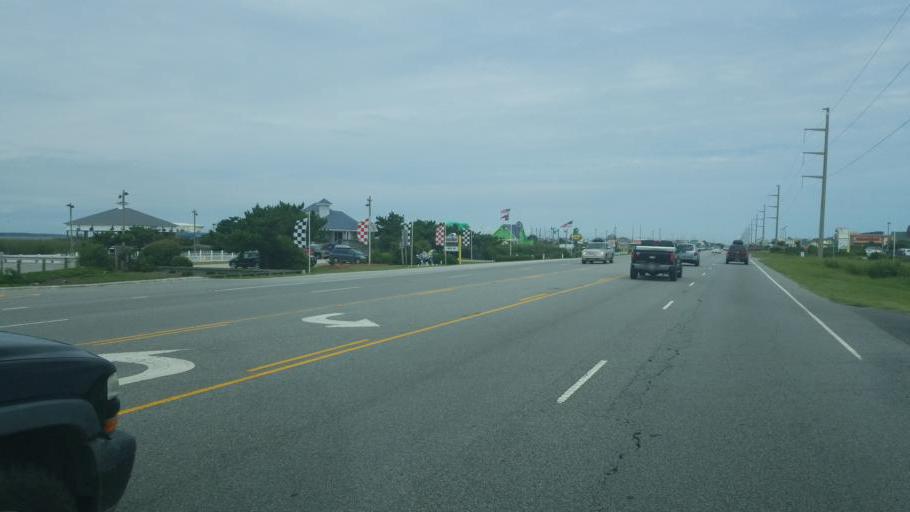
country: US
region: North Carolina
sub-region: Dare County
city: Nags Head
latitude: 35.9137
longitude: -75.6016
